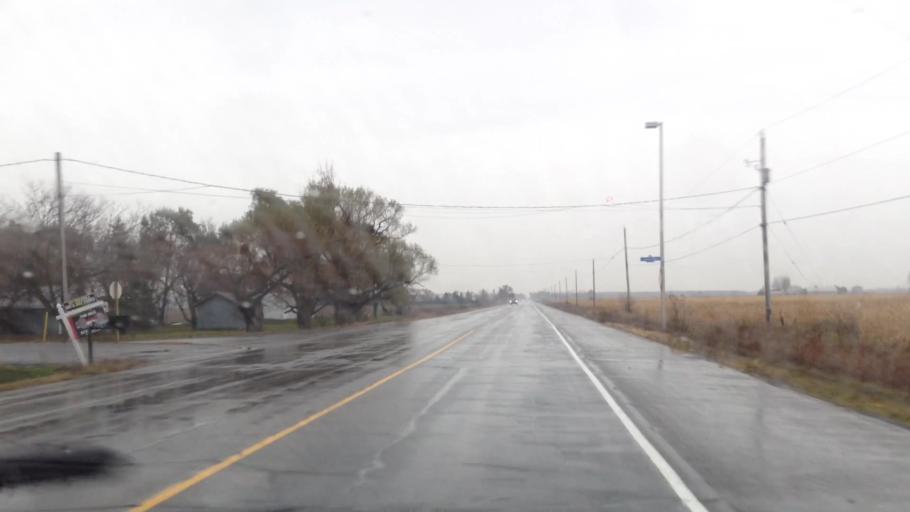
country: CA
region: Ontario
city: Clarence-Rockland
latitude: 45.4596
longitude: -75.4292
